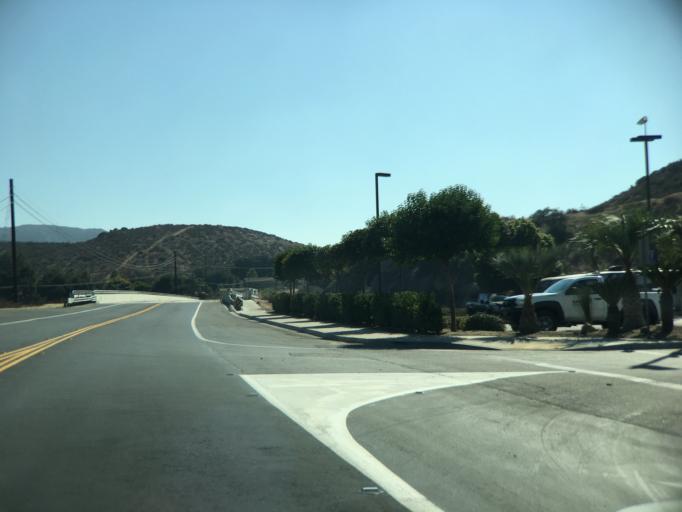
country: US
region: California
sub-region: San Diego County
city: Valley Center
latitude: 33.2653
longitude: -116.9539
